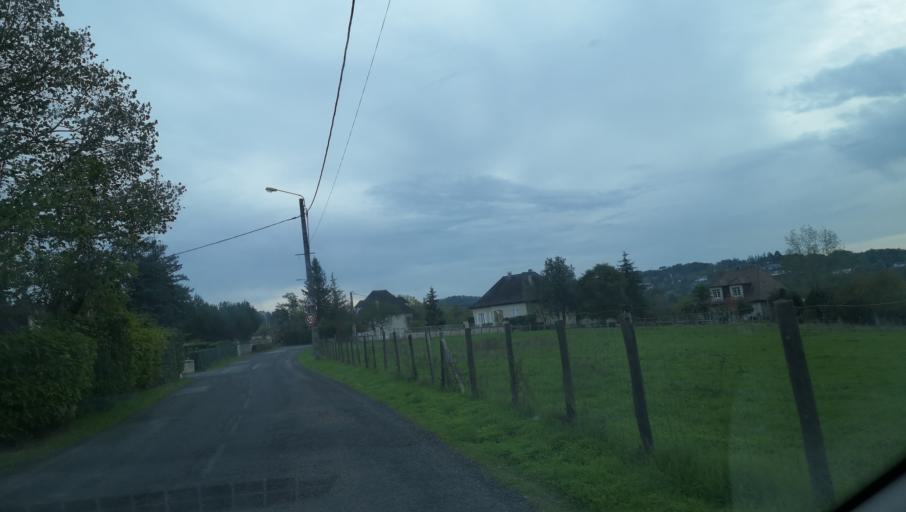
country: FR
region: Limousin
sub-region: Departement de la Correze
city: Brive-la-Gaillarde
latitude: 45.1471
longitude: 1.5490
